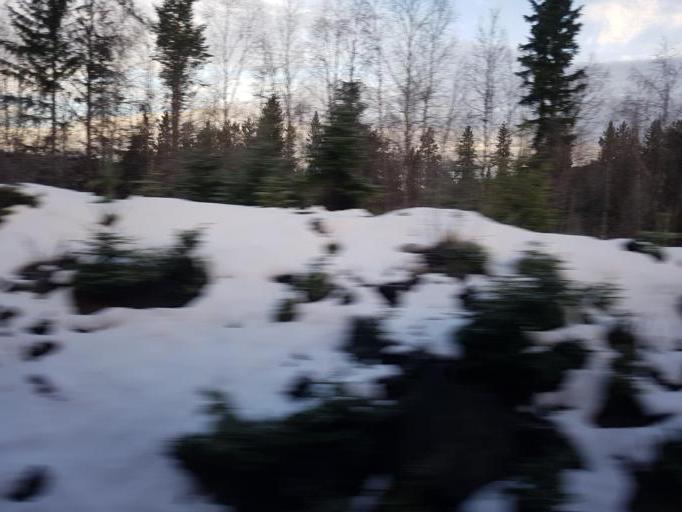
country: NO
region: Sor-Trondelag
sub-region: Rennebu
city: Berkak
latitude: 62.7528
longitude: 9.9852
